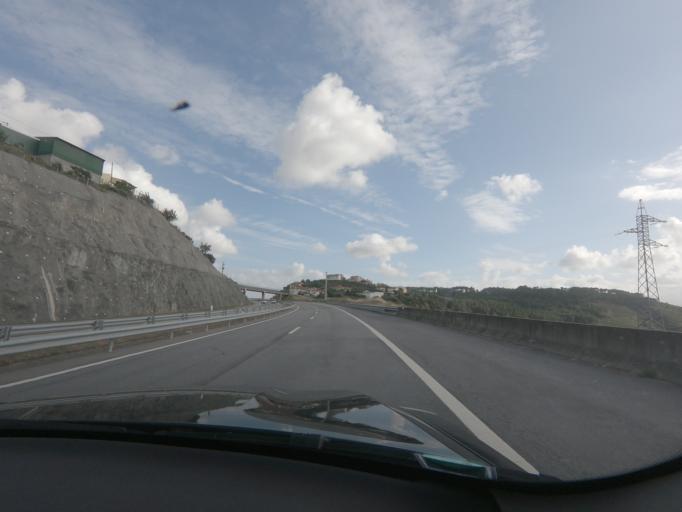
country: PT
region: Vila Real
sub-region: Santa Marta de Penaguiao
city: Santa Marta de Penaguiao
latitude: 41.2266
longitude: -7.7358
